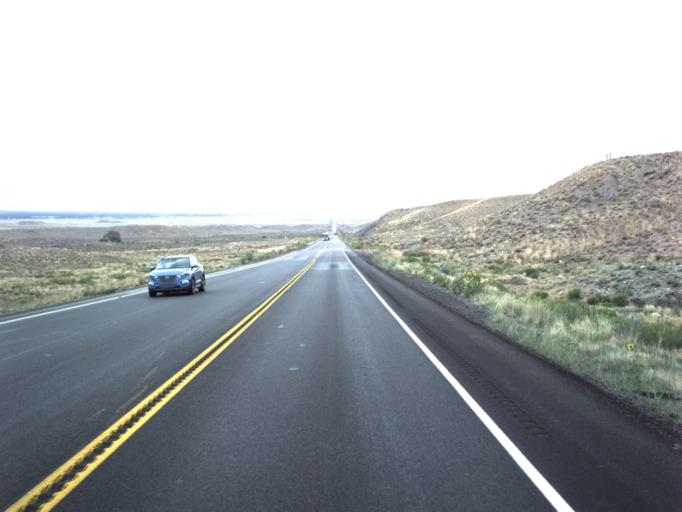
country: US
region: Utah
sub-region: Carbon County
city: East Carbon City
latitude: 39.4754
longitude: -110.5042
